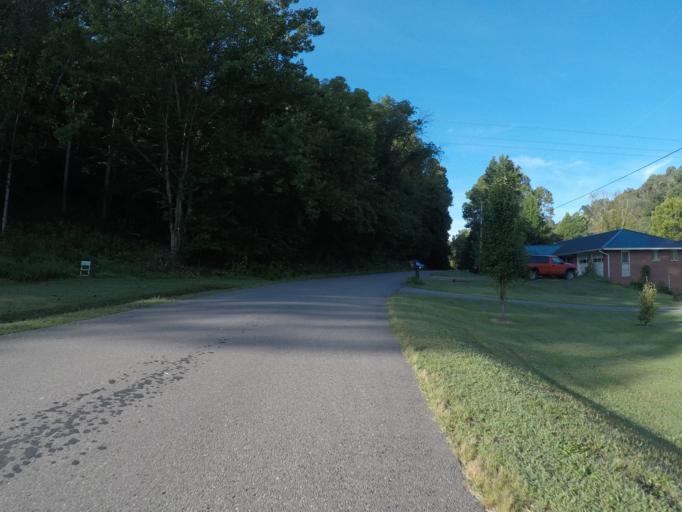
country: US
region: Ohio
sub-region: Lawrence County
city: Coal Grove
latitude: 38.5615
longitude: -82.5503
